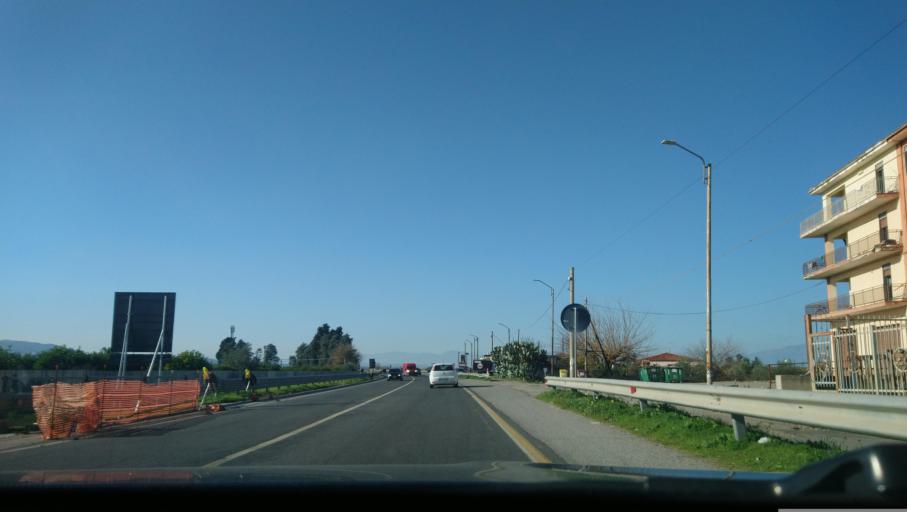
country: IT
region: Calabria
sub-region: Provincia di Cosenza
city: Fabrizio
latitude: 39.6329
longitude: 16.5620
